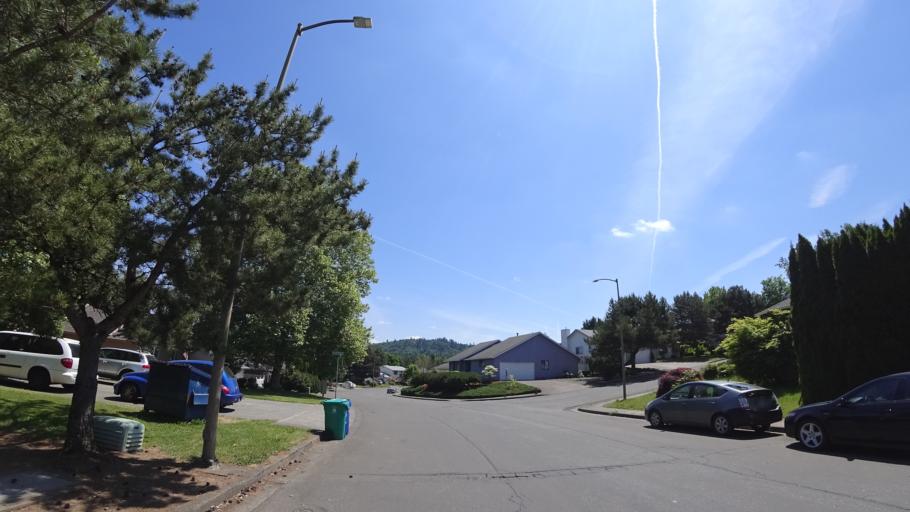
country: US
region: Oregon
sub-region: Clackamas County
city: Happy Valley
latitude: 45.4929
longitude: -122.4923
